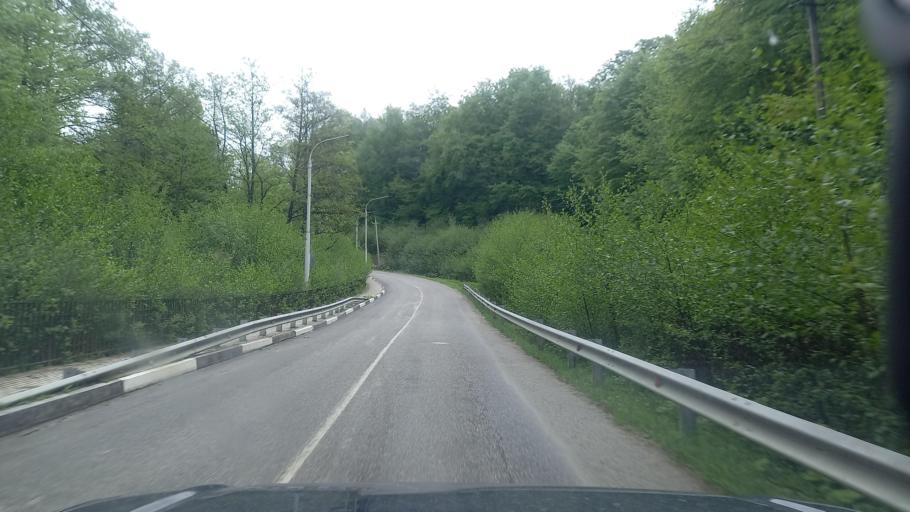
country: RU
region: Kabardino-Balkariya
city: Babugent
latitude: 43.2274
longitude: 43.5541
